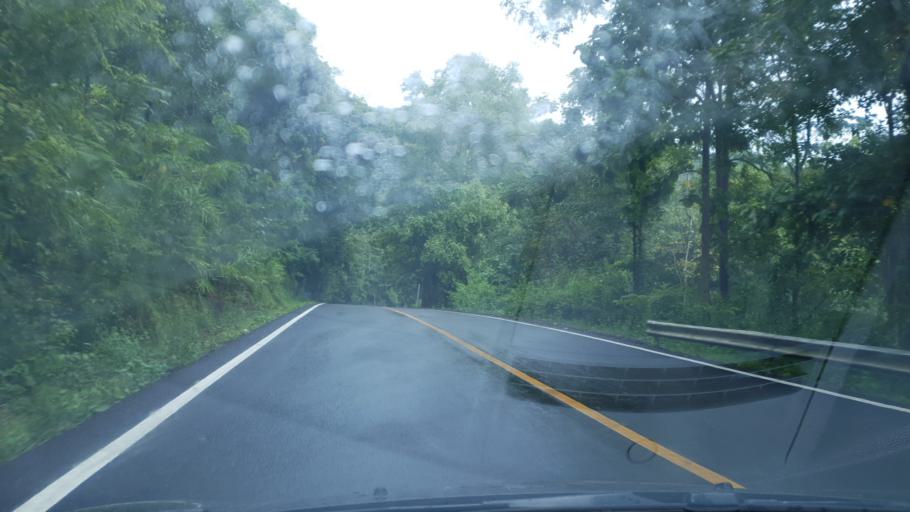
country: TH
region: Mae Hong Son
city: Pa Pae
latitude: 18.2685
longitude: 97.9404
